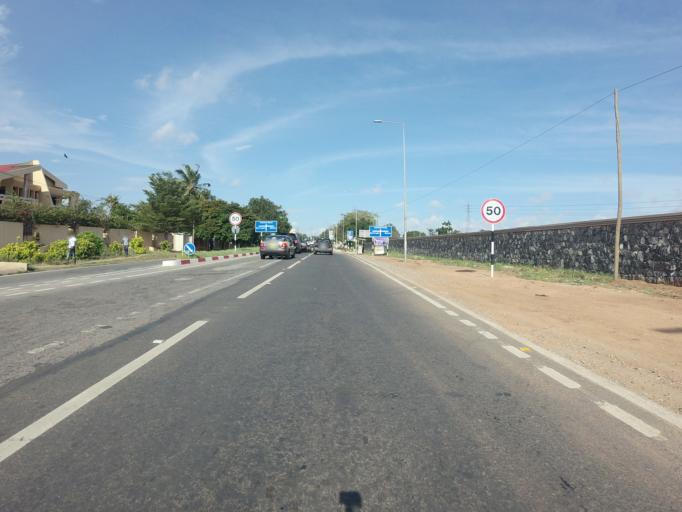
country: GH
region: Greater Accra
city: Medina Estates
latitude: 5.6303
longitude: -0.1586
